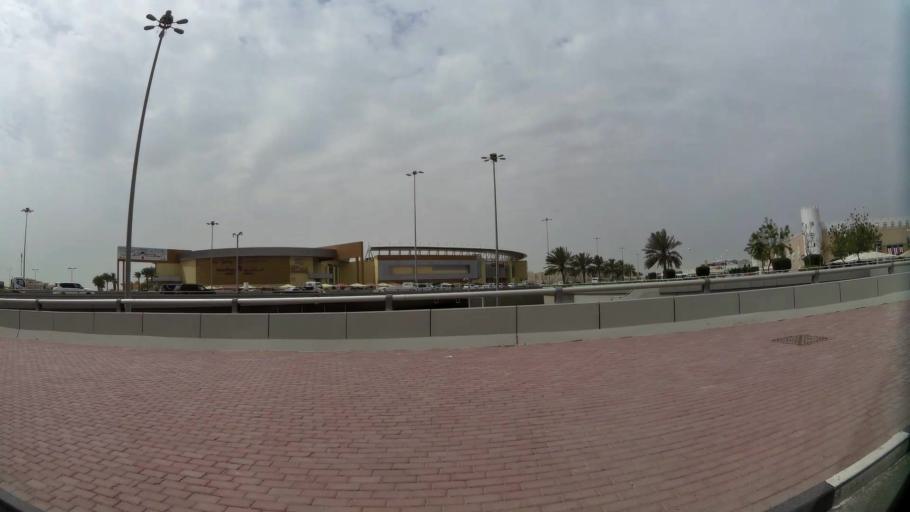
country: QA
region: Baladiyat ar Rayyan
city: Ar Rayyan
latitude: 25.3320
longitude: 51.4651
